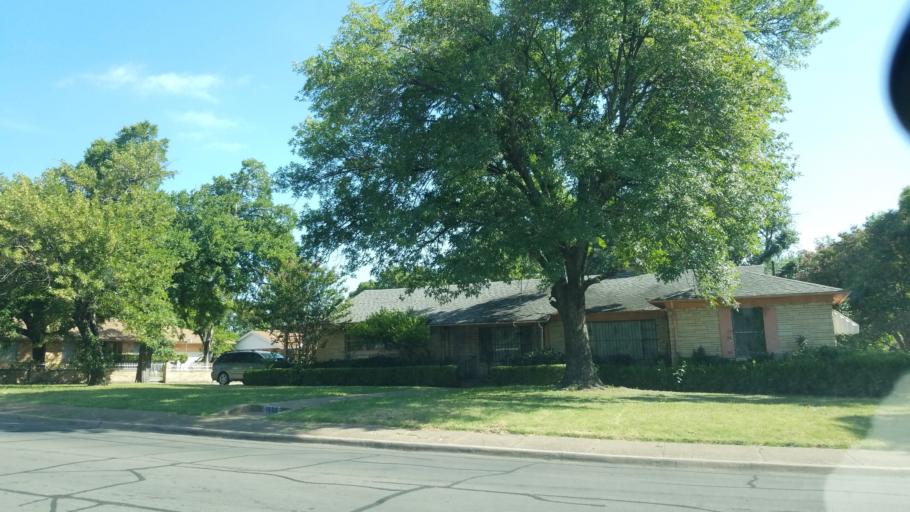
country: US
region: Texas
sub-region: Dallas County
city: Dallas
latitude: 32.7153
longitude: -96.8034
